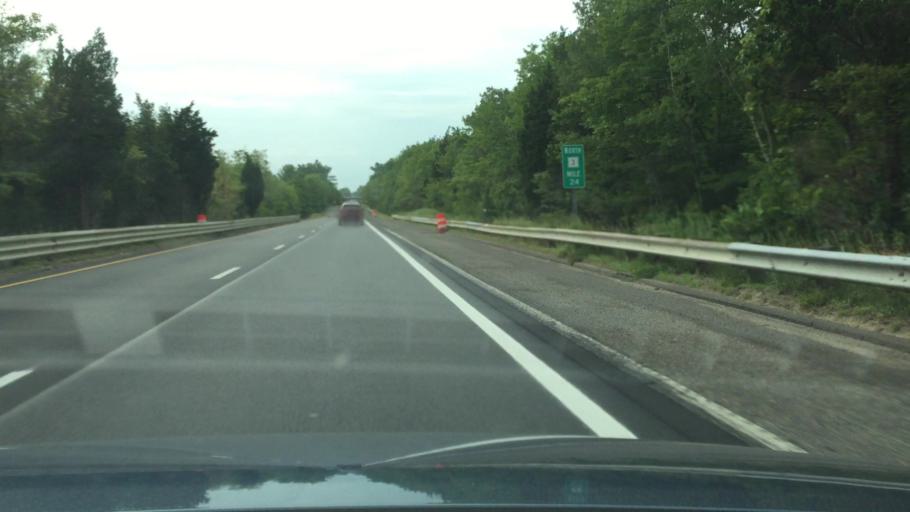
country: US
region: Massachusetts
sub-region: Plymouth County
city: Marshfield
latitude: 42.0752
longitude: -70.7349
